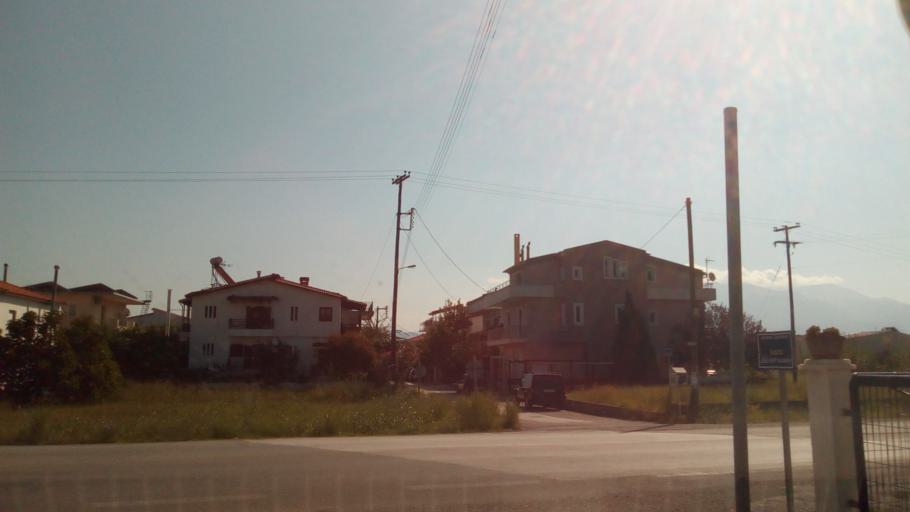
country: GR
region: West Greece
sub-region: Nomos Aitolias kai Akarnanias
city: Antirrio
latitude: 38.3679
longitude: 21.7795
